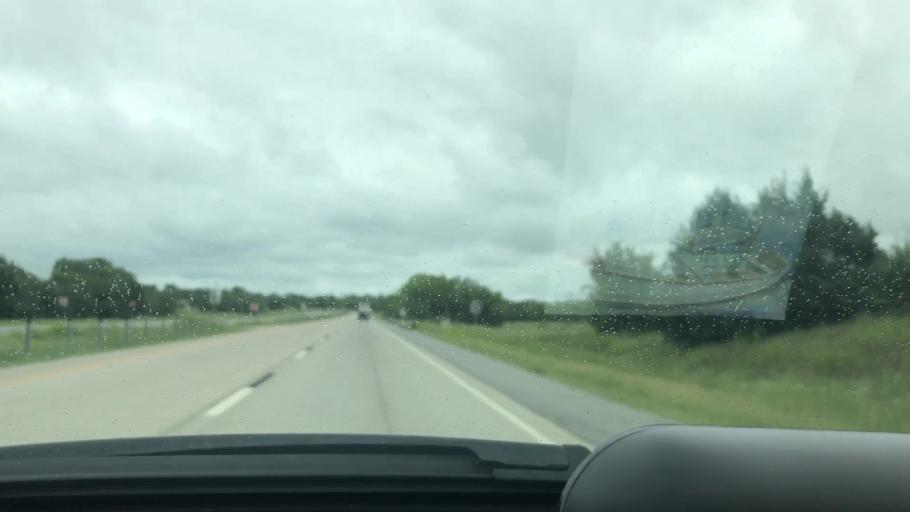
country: US
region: Oklahoma
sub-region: Pittsburg County
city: McAlester
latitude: 34.8179
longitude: -95.8535
